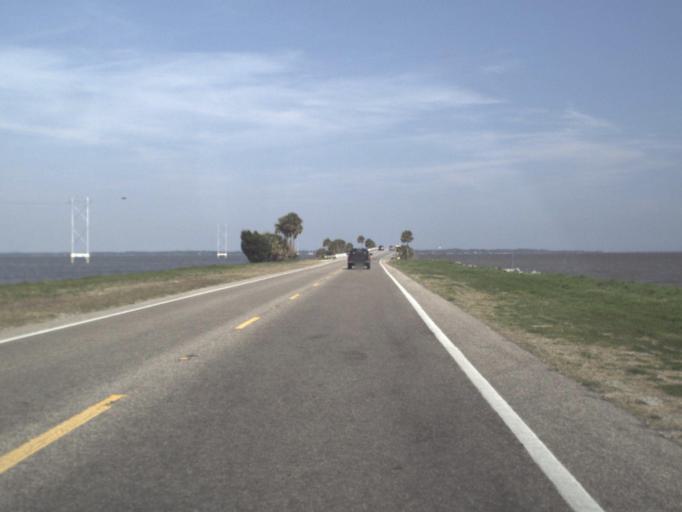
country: US
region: Florida
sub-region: Franklin County
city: Apalachicola
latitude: 29.7276
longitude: -84.9599
